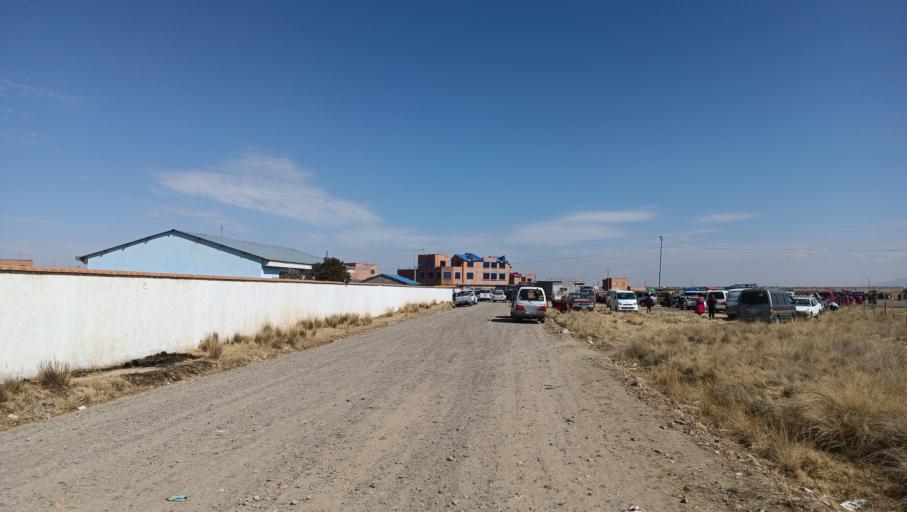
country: BO
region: La Paz
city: Batallas
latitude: -16.4381
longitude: -68.3710
